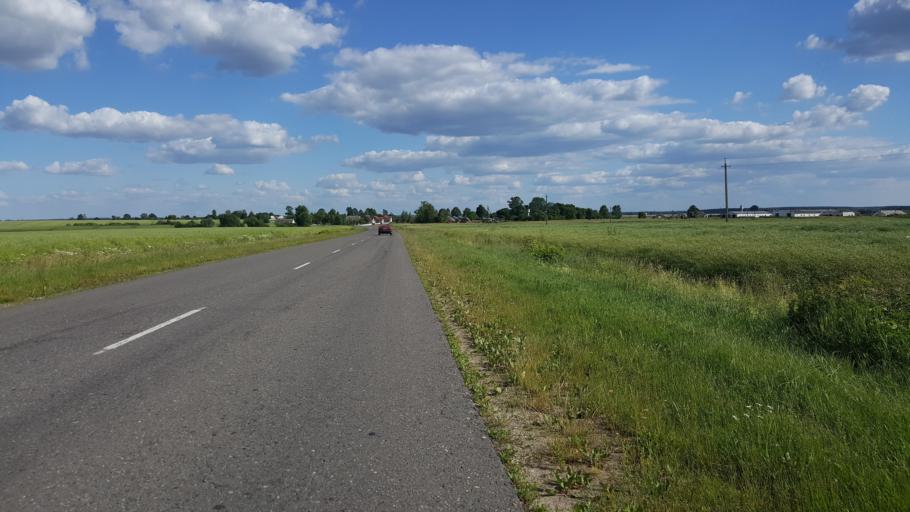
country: BY
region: Brest
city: Kamyanyets
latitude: 52.4373
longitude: 23.7456
